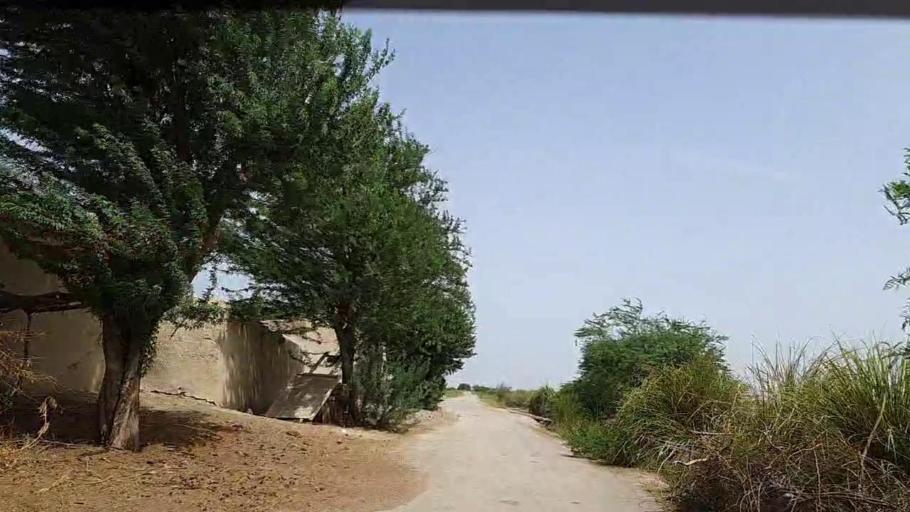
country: PK
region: Sindh
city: Johi
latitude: 26.7816
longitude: 67.6203
